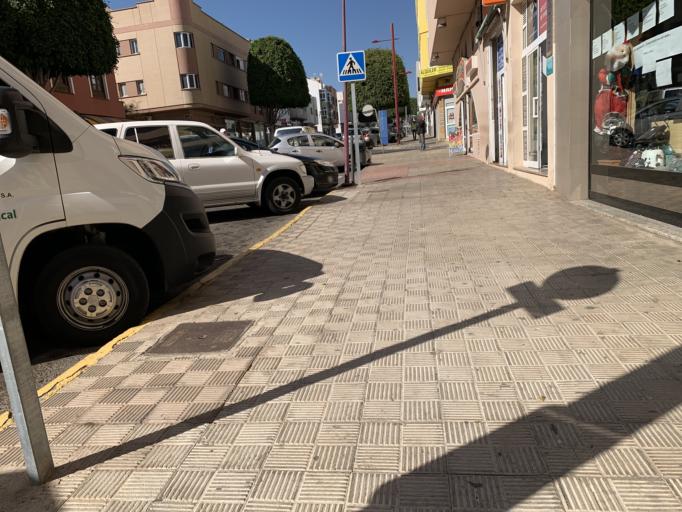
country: ES
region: Canary Islands
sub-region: Provincia de Las Palmas
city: Puerto del Rosario
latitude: 28.5016
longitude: -13.8686
